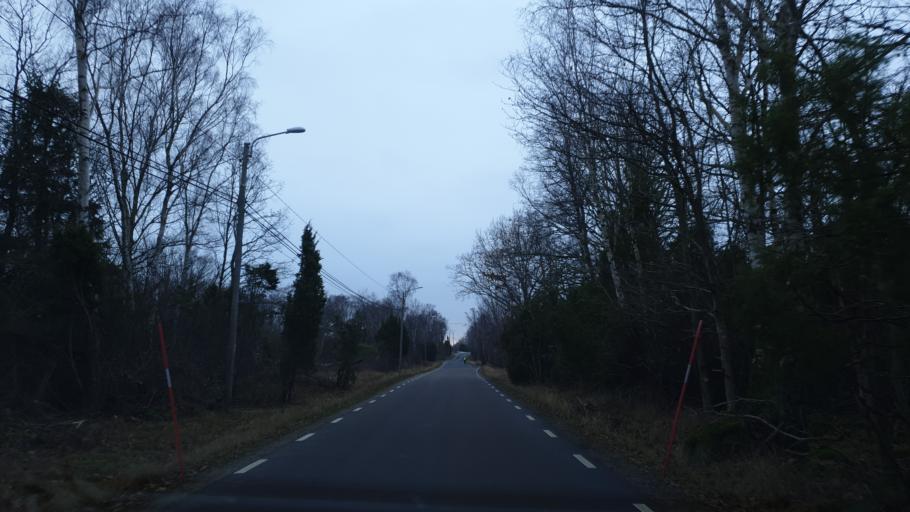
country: SE
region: Blekinge
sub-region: Karlskrona Kommun
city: Karlskrona
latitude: 56.1154
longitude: 15.6145
